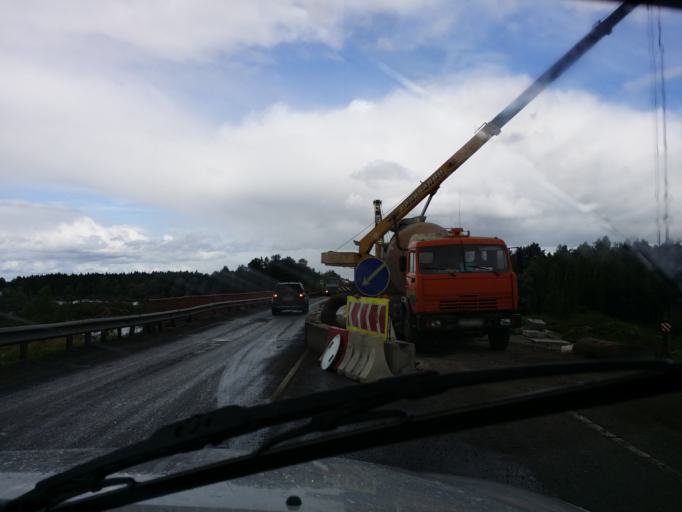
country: RU
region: Tjumen
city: Mendeleyevo
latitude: 58.4490
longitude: 68.4736
